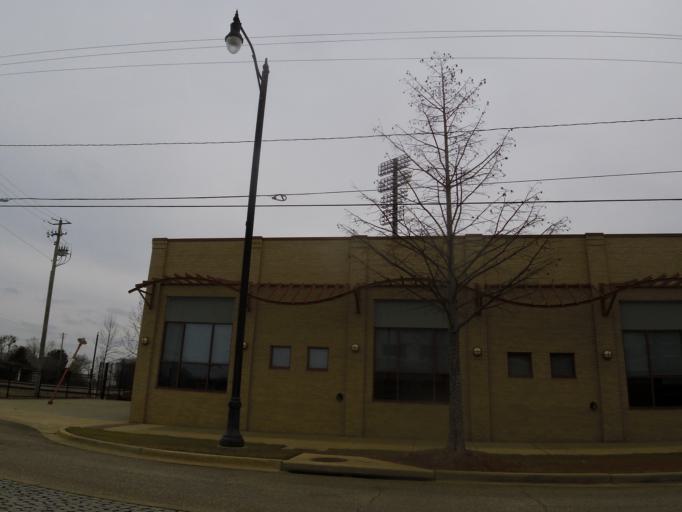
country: US
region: Alabama
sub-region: Montgomery County
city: Montgomery
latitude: 32.3820
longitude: -86.3119
